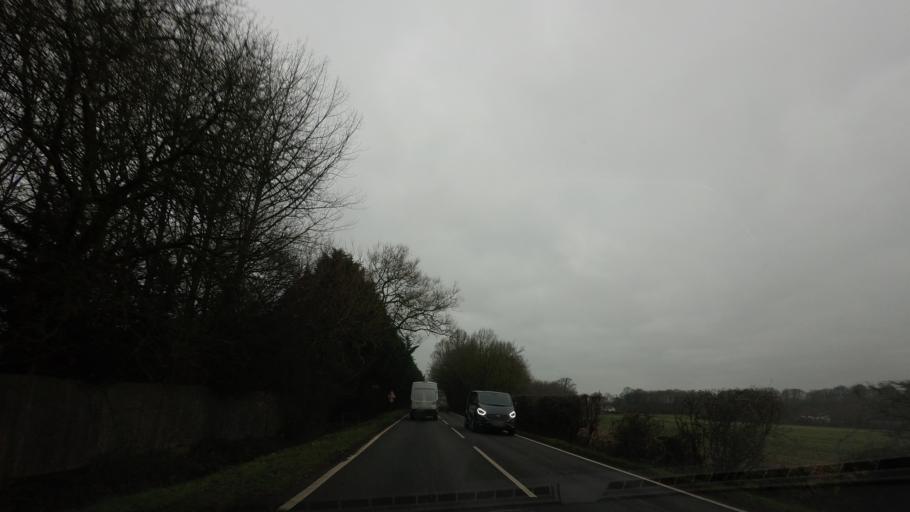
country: GB
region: England
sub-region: Kent
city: Staplehurst
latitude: 51.1435
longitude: 0.5518
